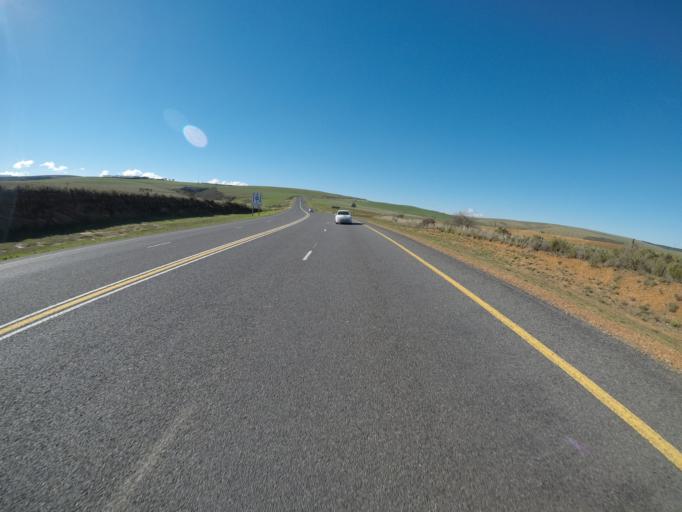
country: ZA
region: Western Cape
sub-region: Overberg District Municipality
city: Caledon
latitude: -34.2347
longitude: 19.2583
